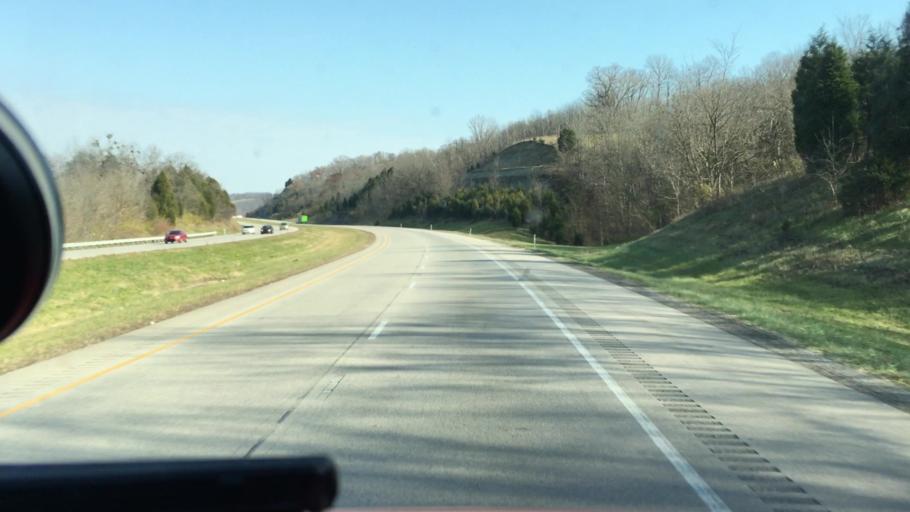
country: US
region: Kentucky
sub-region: Bath County
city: Owingsville
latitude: 38.1052
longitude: -83.8259
